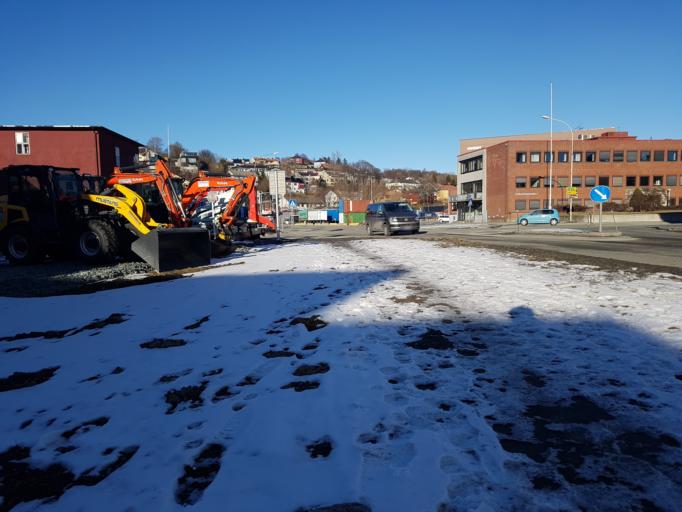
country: NO
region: Sor-Trondelag
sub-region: Trondheim
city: Trondheim
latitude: 63.4419
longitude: 10.4265
